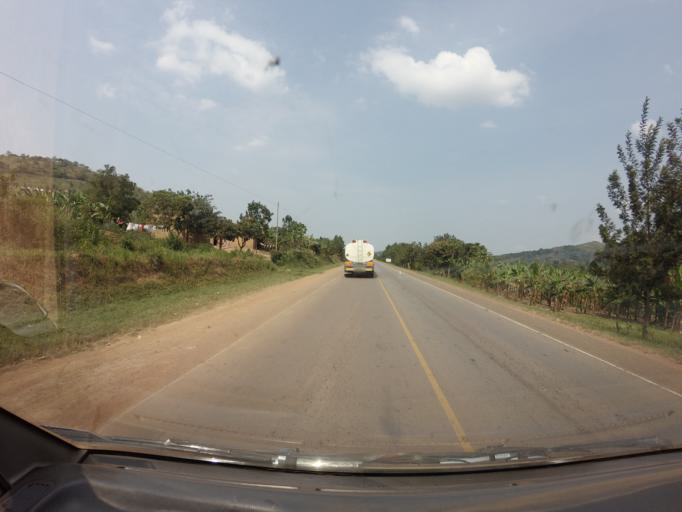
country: UG
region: Central Region
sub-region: Lwengo District
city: Lwengo
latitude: -0.3923
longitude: 31.3297
